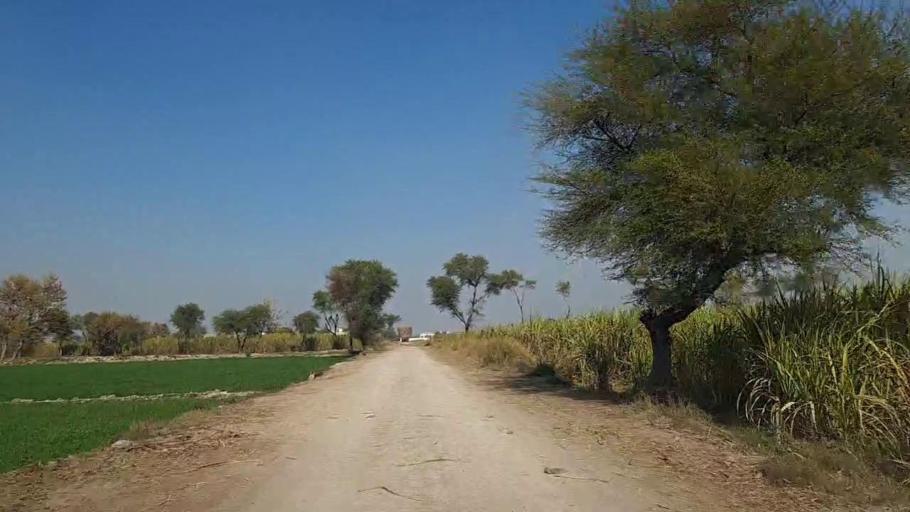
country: PK
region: Sindh
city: Daur
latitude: 26.4995
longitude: 68.3387
